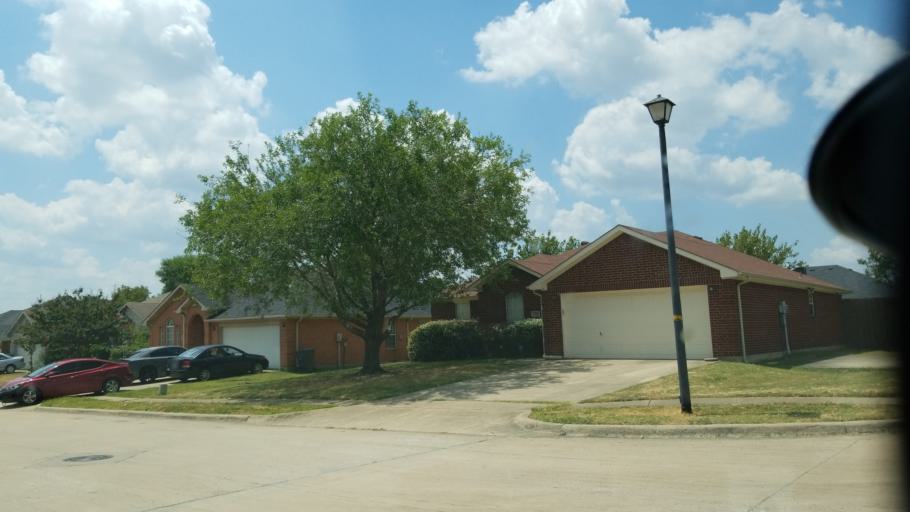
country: US
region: Texas
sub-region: Dallas County
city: Duncanville
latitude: 32.6814
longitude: -96.8963
